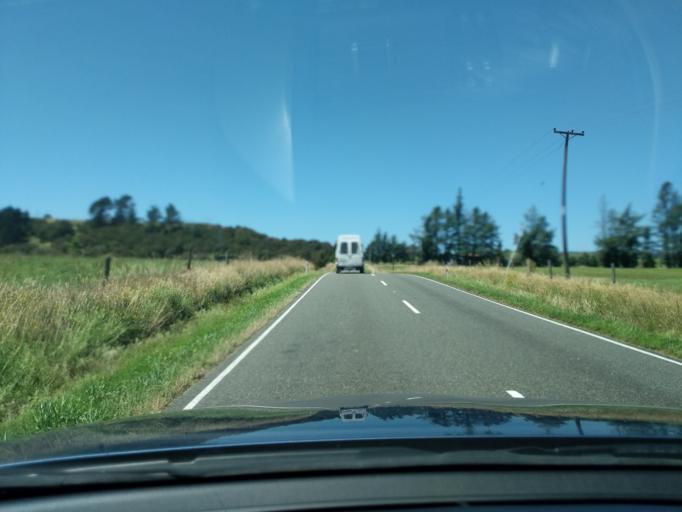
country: NZ
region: Tasman
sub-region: Tasman District
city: Takaka
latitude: -40.6949
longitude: 172.6351
